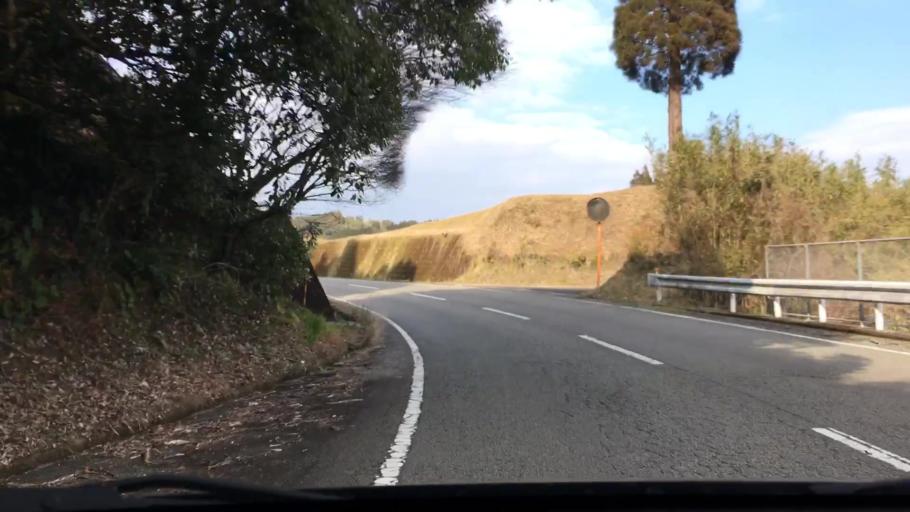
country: JP
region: Miyazaki
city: Nichinan
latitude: 31.5916
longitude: 131.3072
